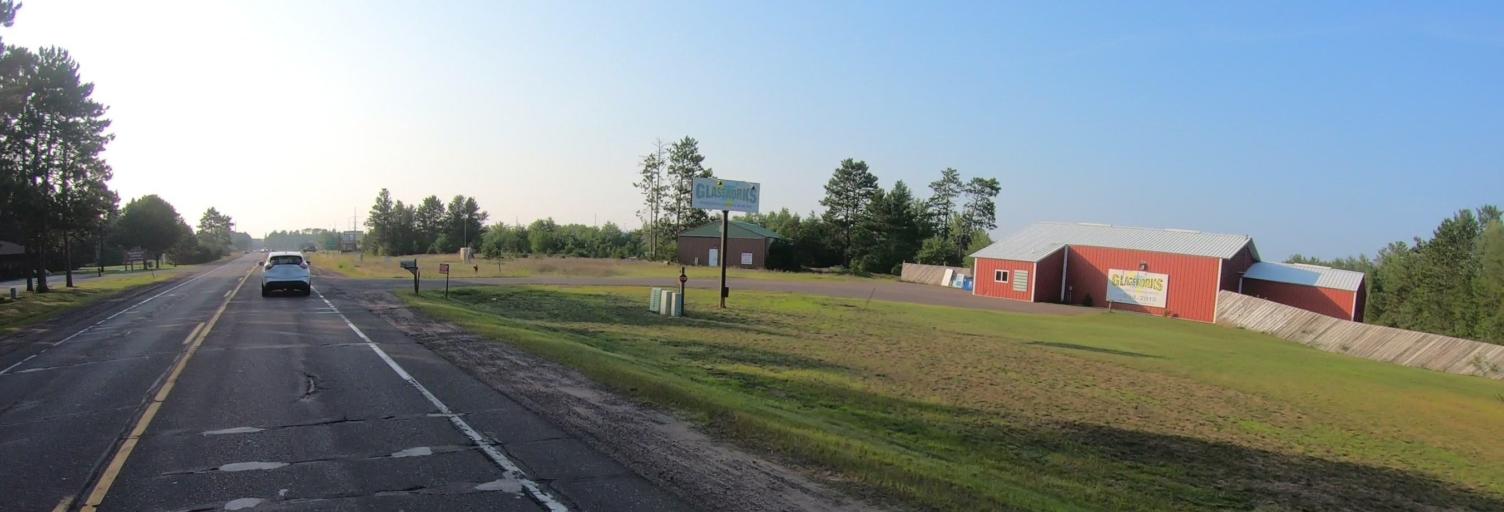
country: US
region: Wisconsin
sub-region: Sawyer County
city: Hayward
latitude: 46.0143
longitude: -91.4692
